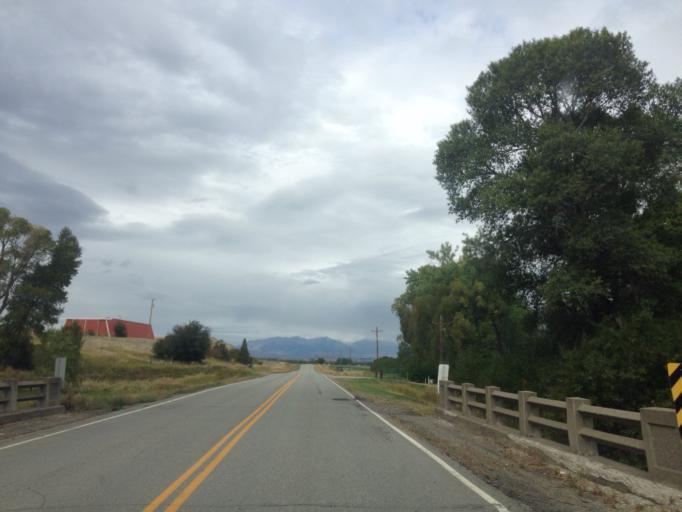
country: US
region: Montana
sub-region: Sweet Grass County
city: Big Timber
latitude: 45.7757
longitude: -109.8058
